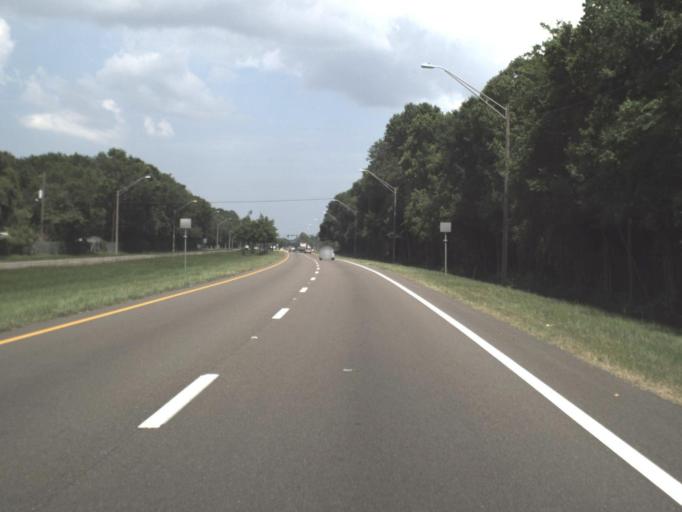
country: US
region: Florida
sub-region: Duval County
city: Jacksonville
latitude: 30.3567
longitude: -81.7058
